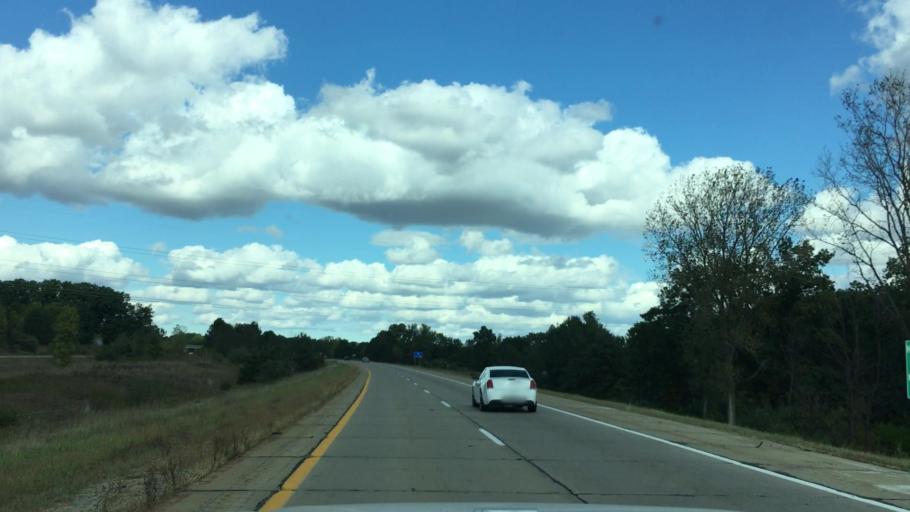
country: US
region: Michigan
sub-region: Eaton County
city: Olivet
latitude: 42.4182
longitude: -84.9609
